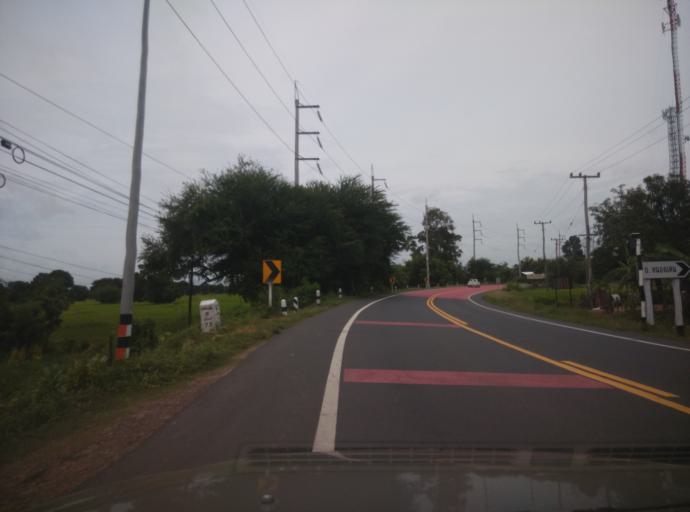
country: TH
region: Sisaket
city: Uthumphon Phisai
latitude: 15.0743
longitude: 104.1000
